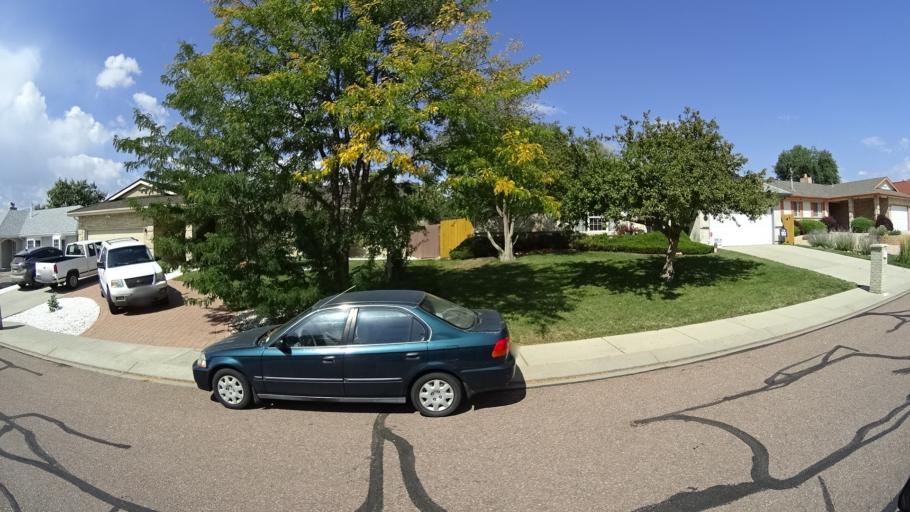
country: US
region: Colorado
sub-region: El Paso County
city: Cimarron Hills
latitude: 38.8638
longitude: -104.7280
